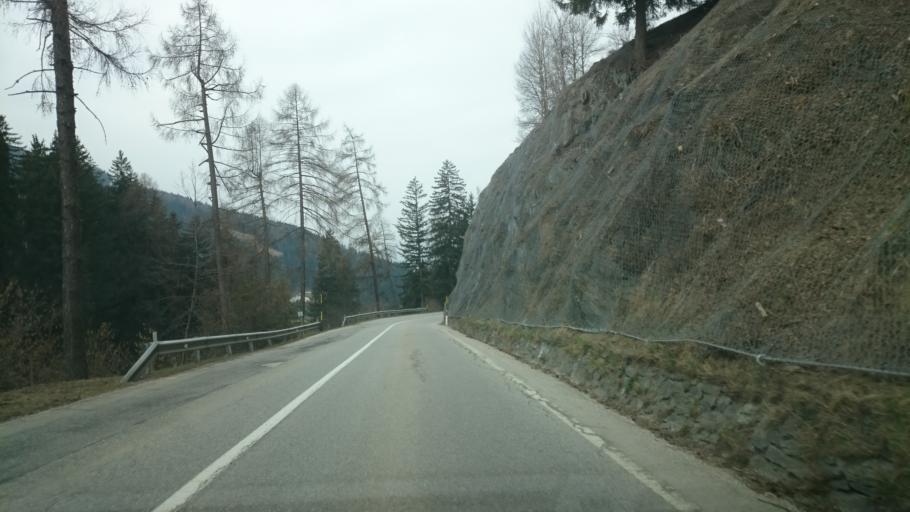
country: IT
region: Trentino-Alto Adige
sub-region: Bolzano
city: Monguelfo
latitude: 46.7605
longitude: 12.0979
